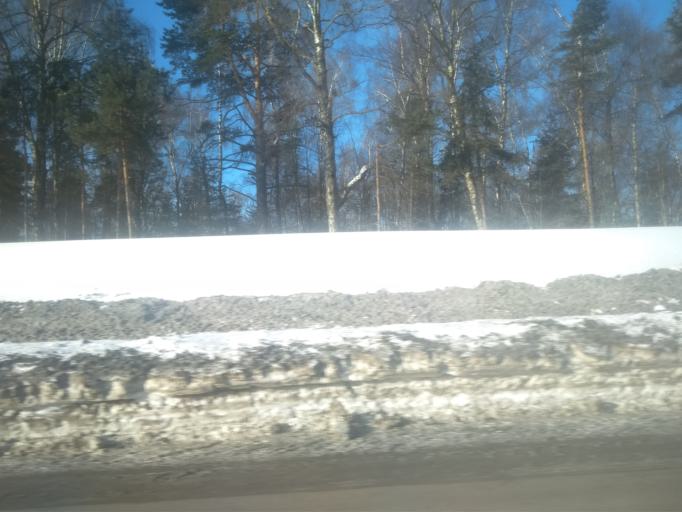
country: RU
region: Moskovskaya
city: Gorki-Leninskiye
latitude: 55.5111
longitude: 37.8311
